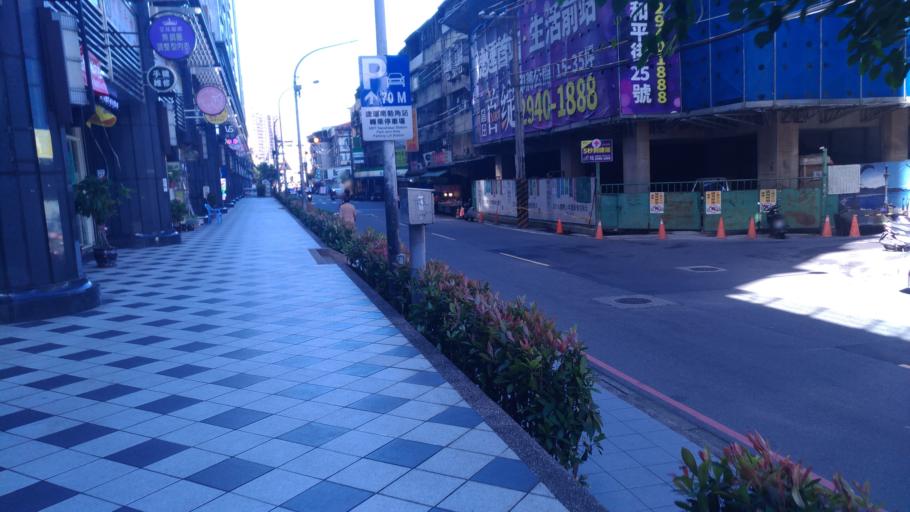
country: TW
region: Taipei
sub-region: Taipei
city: Banqiao
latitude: 24.9903
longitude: 121.5093
